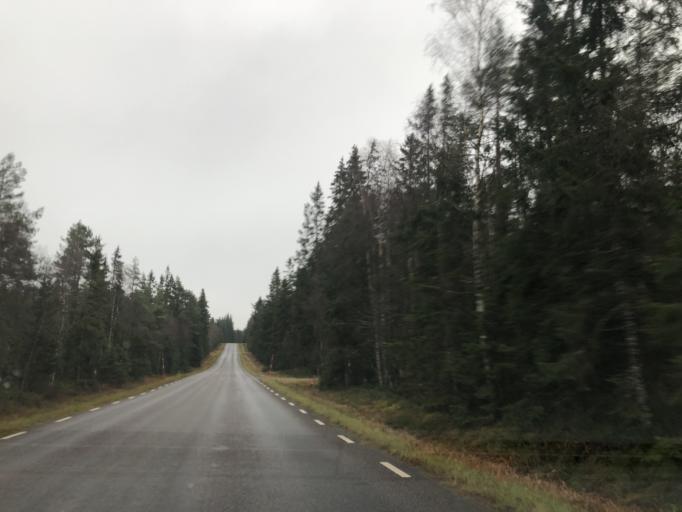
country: SE
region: Vaestra Goetaland
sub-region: Ulricehamns Kommun
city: Ulricehamn
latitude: 57.7416
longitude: 13.5371
